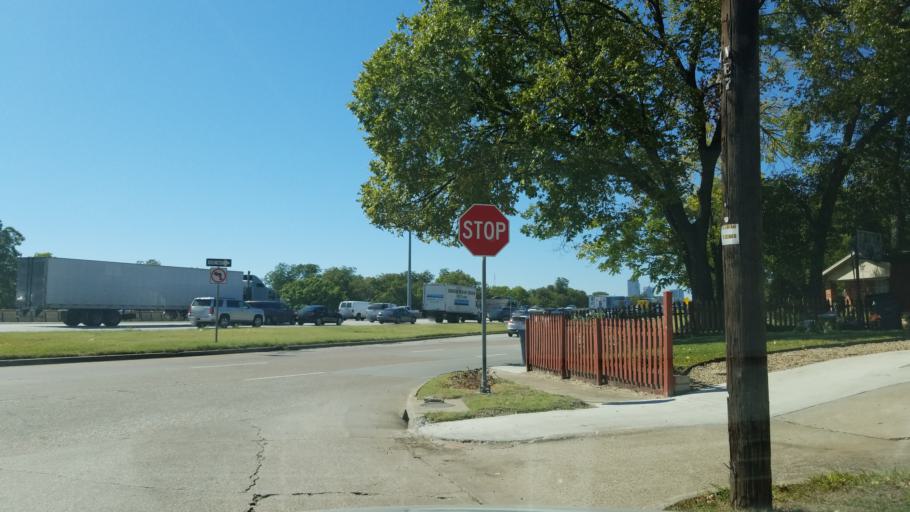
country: US
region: Texas
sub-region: Dallas County
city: Dallas
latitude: 32.7916
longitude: -96.7534
